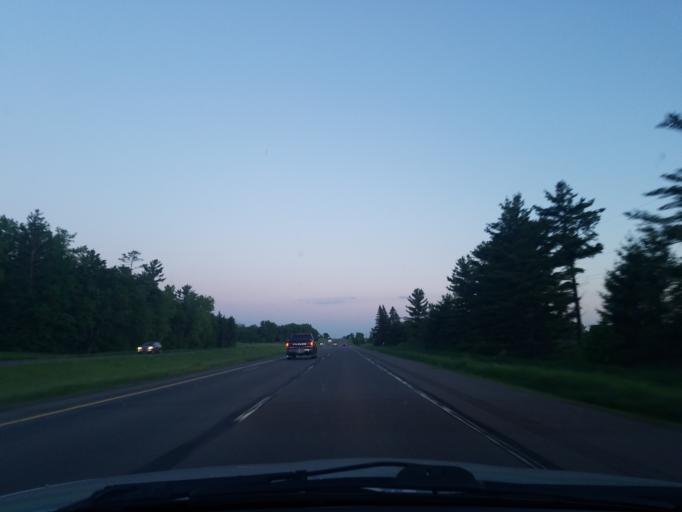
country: US
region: Minnesota
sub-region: Pine County
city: Pine City
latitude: 45.7938
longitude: -92.9906
